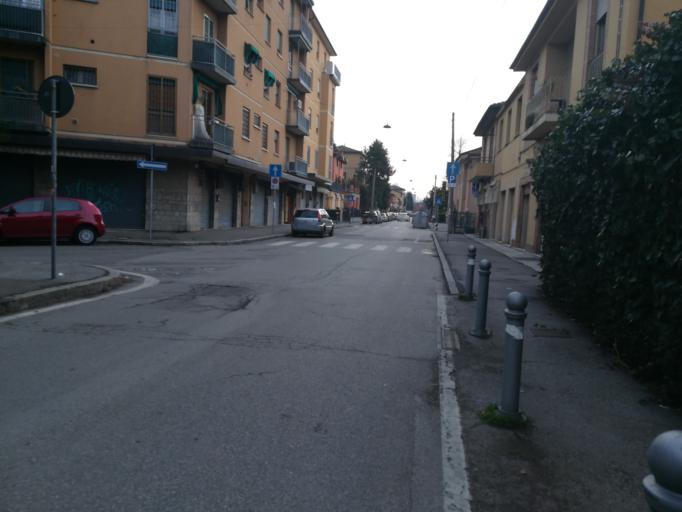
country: IT
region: Emilia-Romagna
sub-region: Provincia di Bologna
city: Progresso
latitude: 44.5486
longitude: 11.3548
